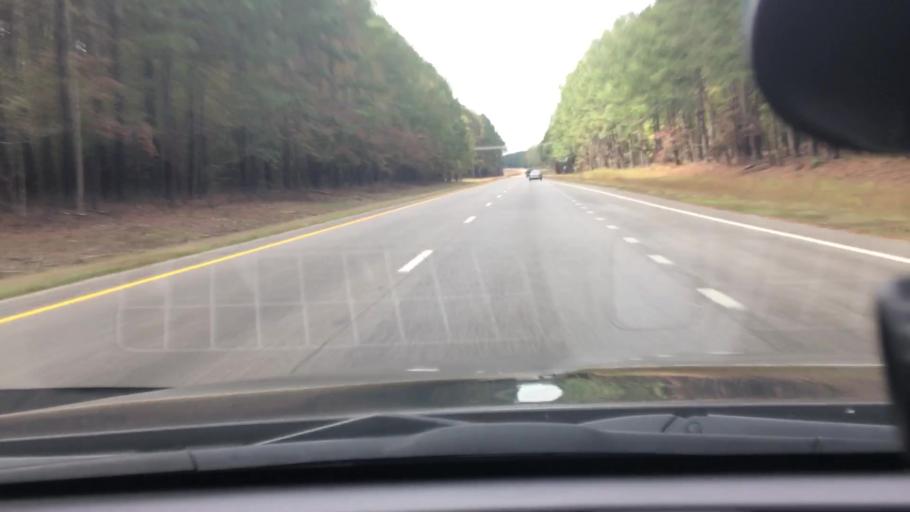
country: US
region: North Carolina
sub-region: Wake County
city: Zebulon
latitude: 35.8016
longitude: -78.1961
